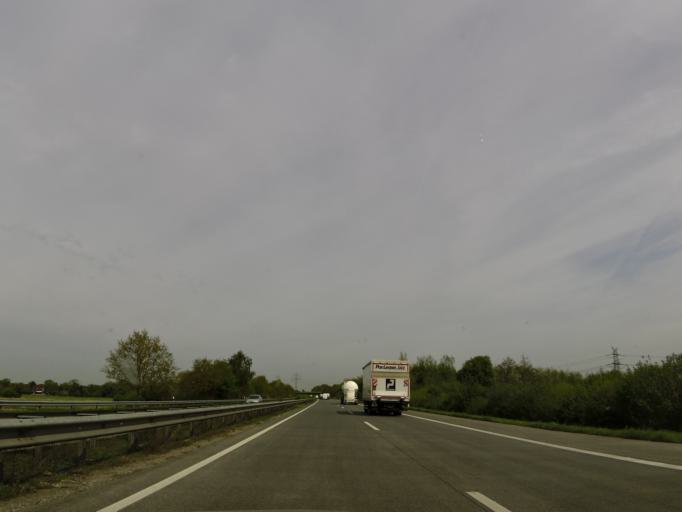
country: DE
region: Schleswig-Holstein
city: Kolln-Reisiek
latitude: 53.7727
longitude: 9.7074
